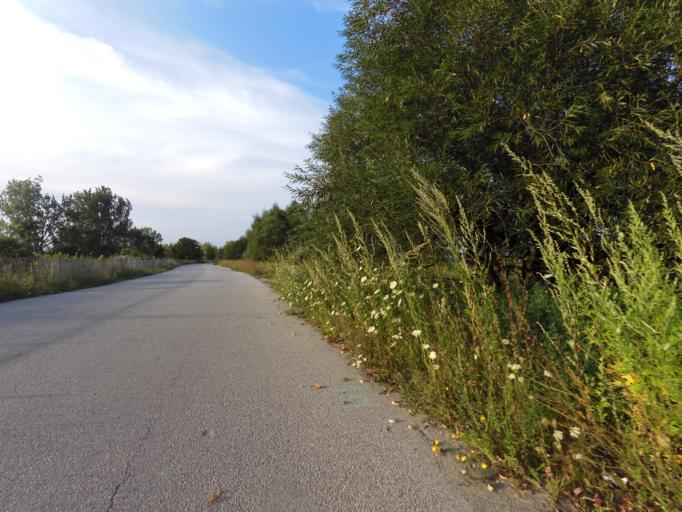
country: CA
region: Ontario
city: Toronto
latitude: 43.6406
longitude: -79.3220
